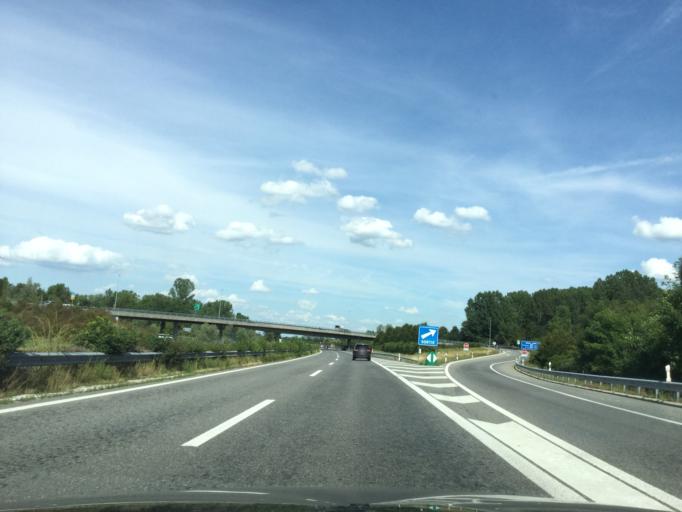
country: CH
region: Fribourg
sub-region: Broye District
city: Cugy
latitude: 46.8266
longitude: 6.9052
